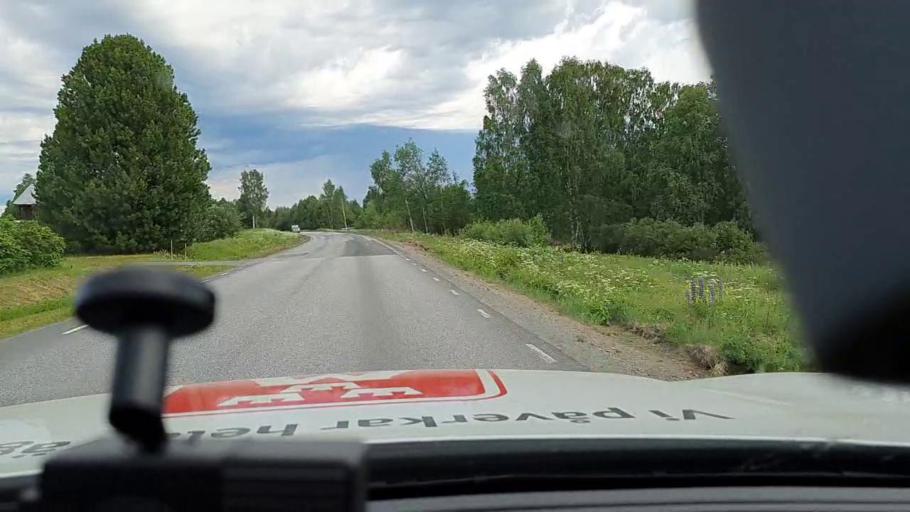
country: SE
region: Norrbotten
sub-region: Bodens Kommun
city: Saevast
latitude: 65.7669
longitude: 21.6906
